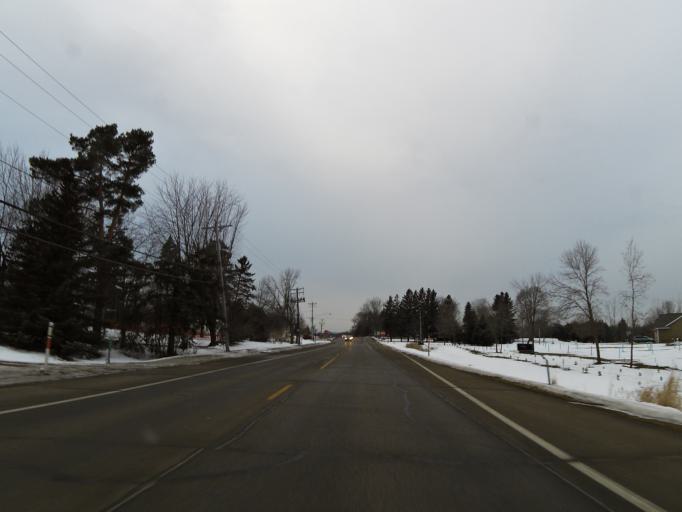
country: US
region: Minnesota
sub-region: Washington County
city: Oakdale
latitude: 44.9923
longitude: -92.9319
